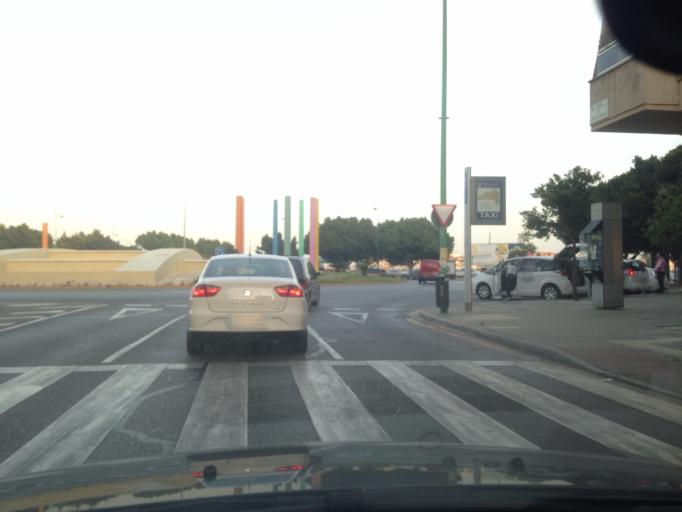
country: ES
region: Andalusia
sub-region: Provincia de Malaga
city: Malaga
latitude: 36.7198
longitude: -4.4607
